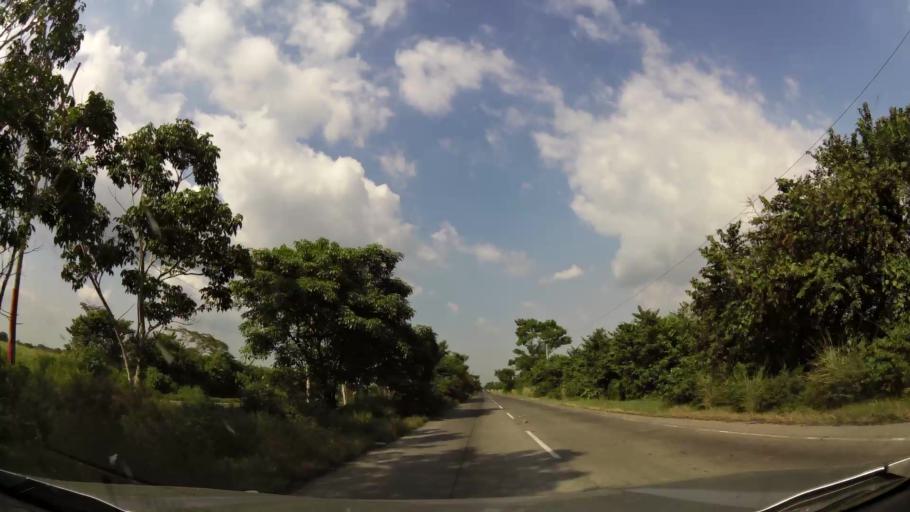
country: GT
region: Escuintla
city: Puerto San Jose
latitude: 14.0292
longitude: -90.7812
